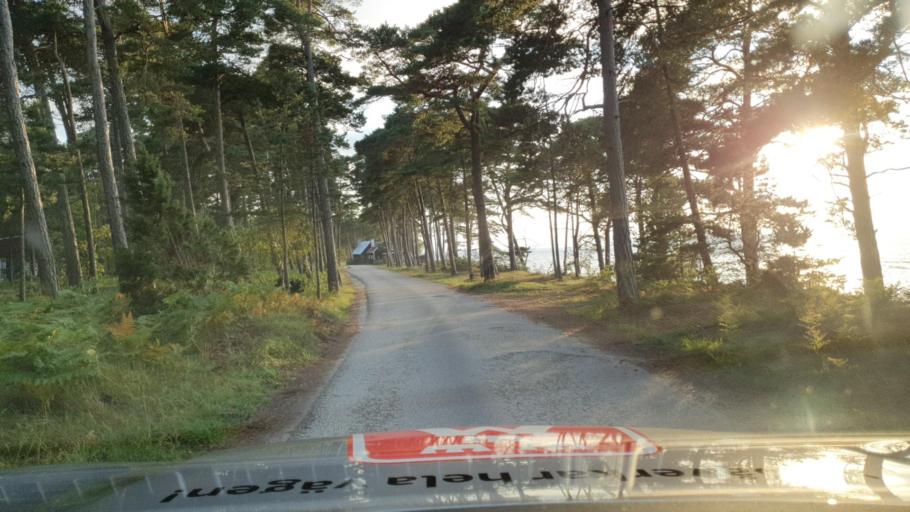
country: SE
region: Gotland
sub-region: Gotland
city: Klintehamn
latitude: 57.3151
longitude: 18.1626
